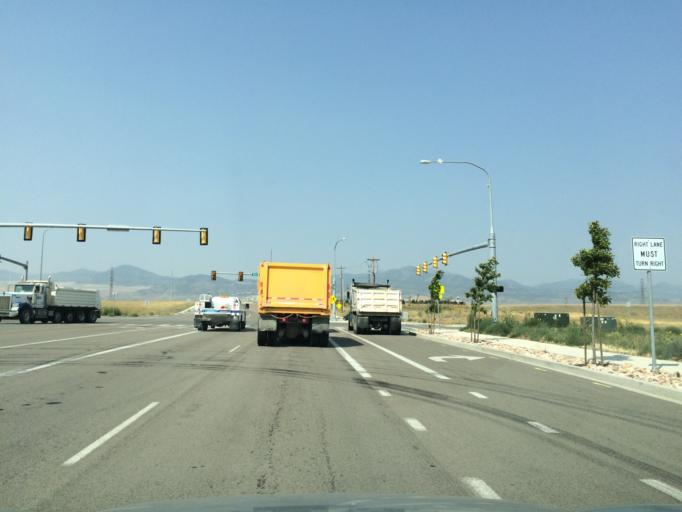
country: US
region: Utah
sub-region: Salt Lake County
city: Oquirrh
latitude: 40.5879
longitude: -112.0234
